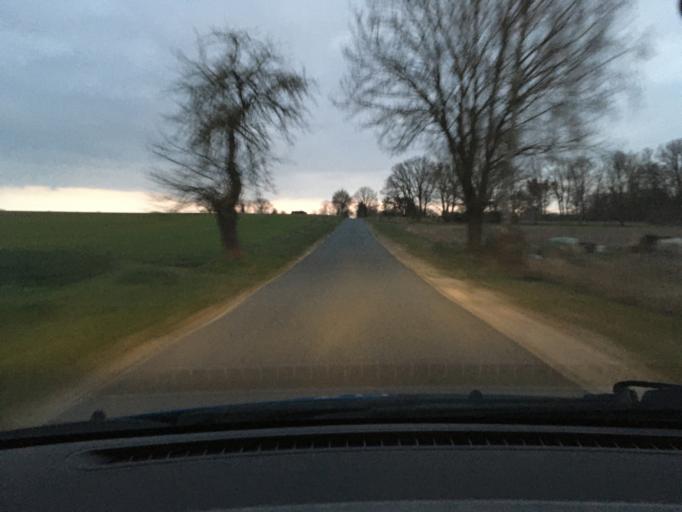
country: DE
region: Lower Saxony
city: Thomasburg
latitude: 53.2299
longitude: 10.6315
